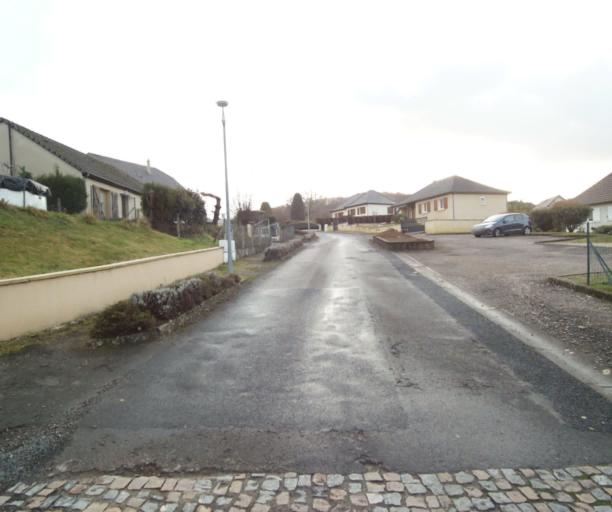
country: FR
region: Limousin
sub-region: Departement de la Correze
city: Cornil
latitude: 45.2071
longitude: 1.6922
